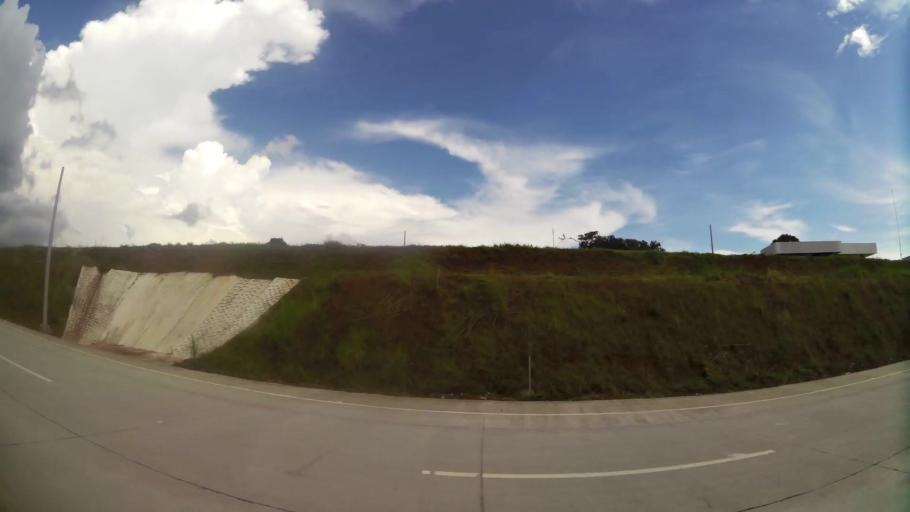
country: PA
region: Panama
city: San Miguelito
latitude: 9.0864
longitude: -79.4430
